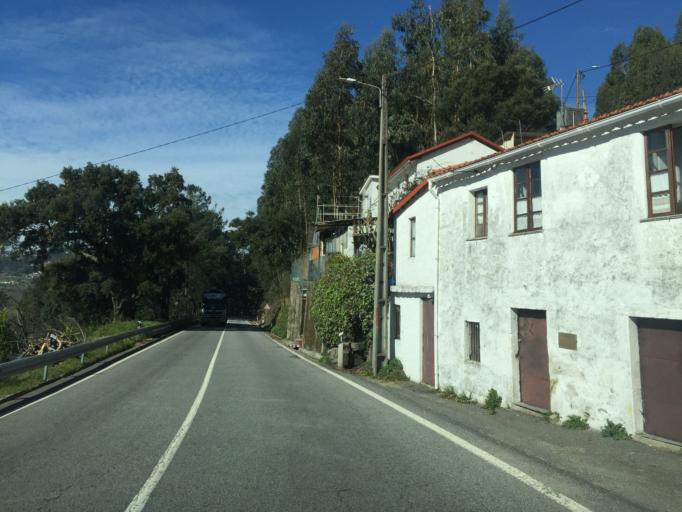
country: PT
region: Aveiro
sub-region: Vale de Cambra
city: Macieira de Cambra
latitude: 40.8983
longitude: -8.3288
